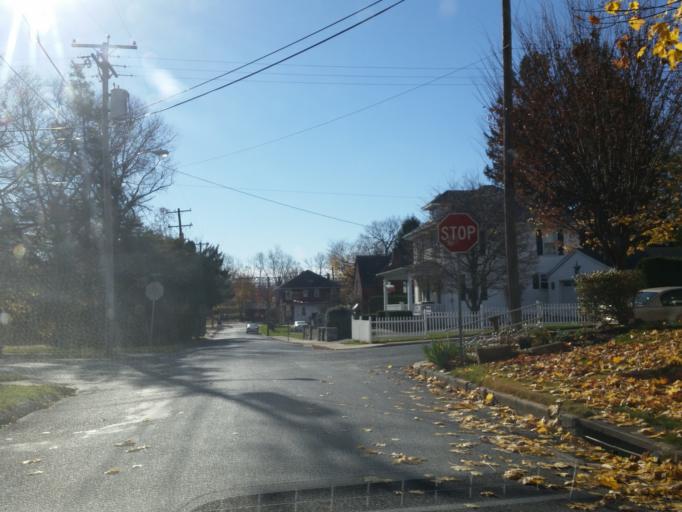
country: US
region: Pennsylvania
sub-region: Lebanon County
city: Annville
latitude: 40.3318
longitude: -76.5102
